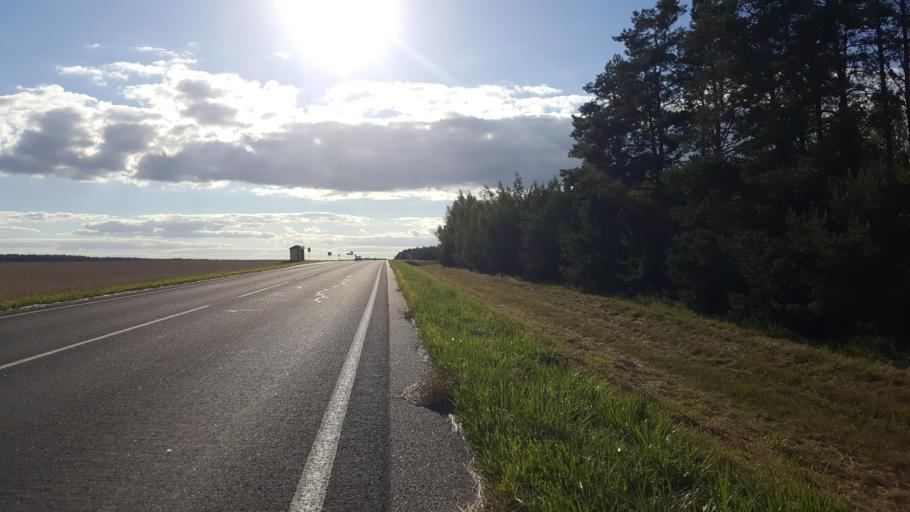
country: BY
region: Brest
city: Kamyanyets
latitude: 52.3929
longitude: 23.9565
